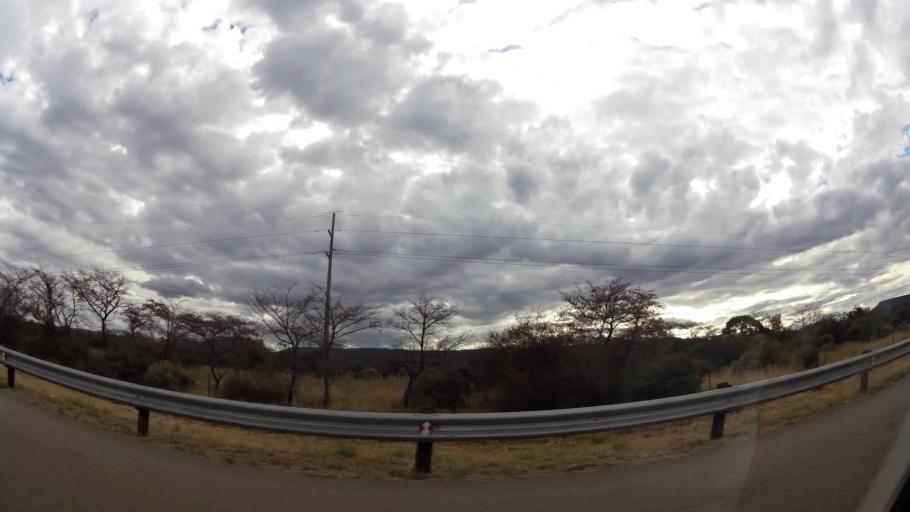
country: ZA
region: Limpopo
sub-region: Waterberg District Municipality
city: Modimolle
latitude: -24.5479
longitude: 28.6878
